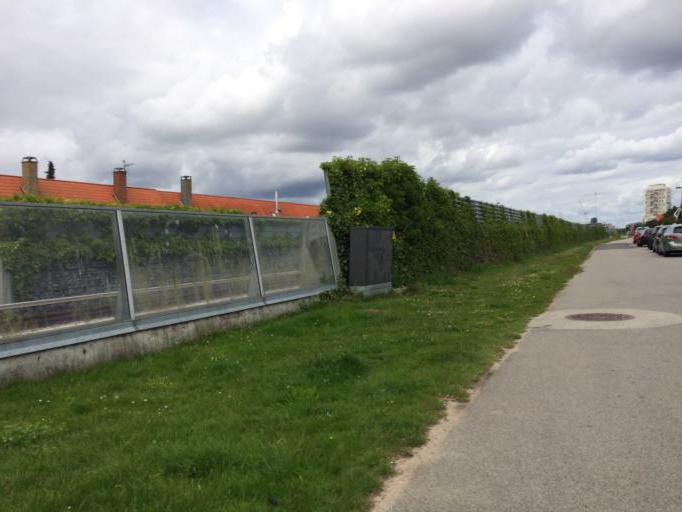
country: DK
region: Capital Region
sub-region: Tarnby Kommune
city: Tarnby
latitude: 55.6533
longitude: 12.6337
